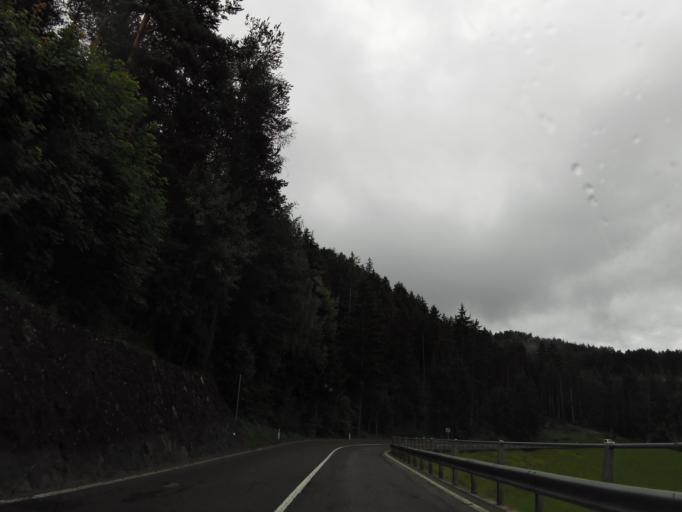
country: IT
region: Trentino-Alto Adige
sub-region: Bolzano
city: Siusi
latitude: 46.5324
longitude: 11.5389
